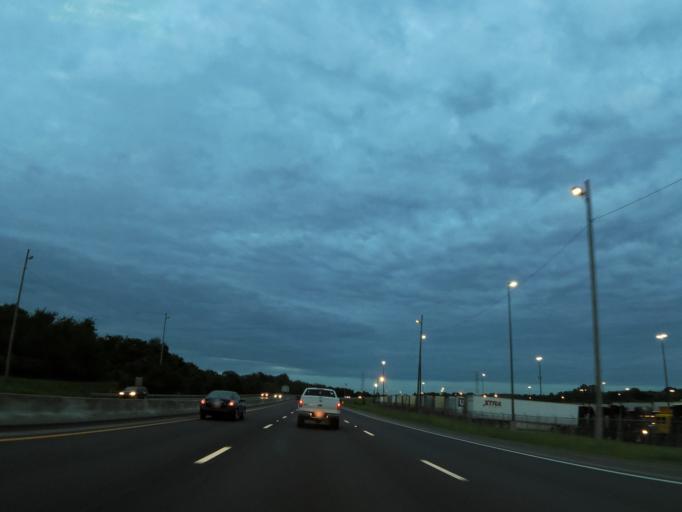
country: US
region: Tennessee
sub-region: Davidson County
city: Nashville
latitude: 36.2343
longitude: -86.8119
